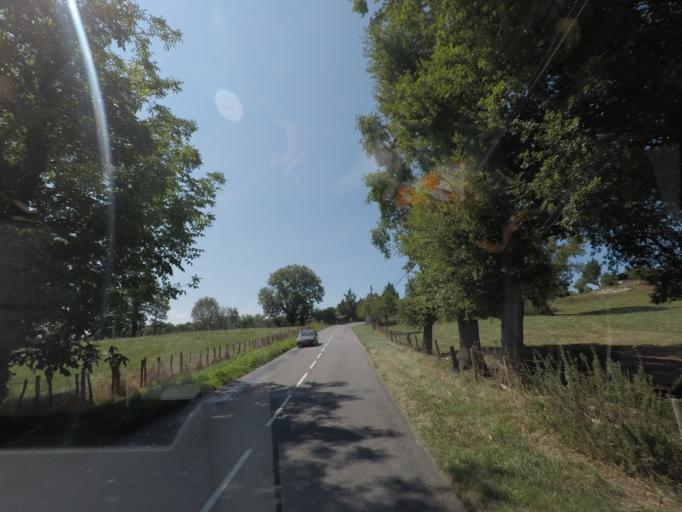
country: FR
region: Midi-Pyrenees
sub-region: Departement de l'Aveyron
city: Capdenac-Gare
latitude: 44.6194
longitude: 2.1118
